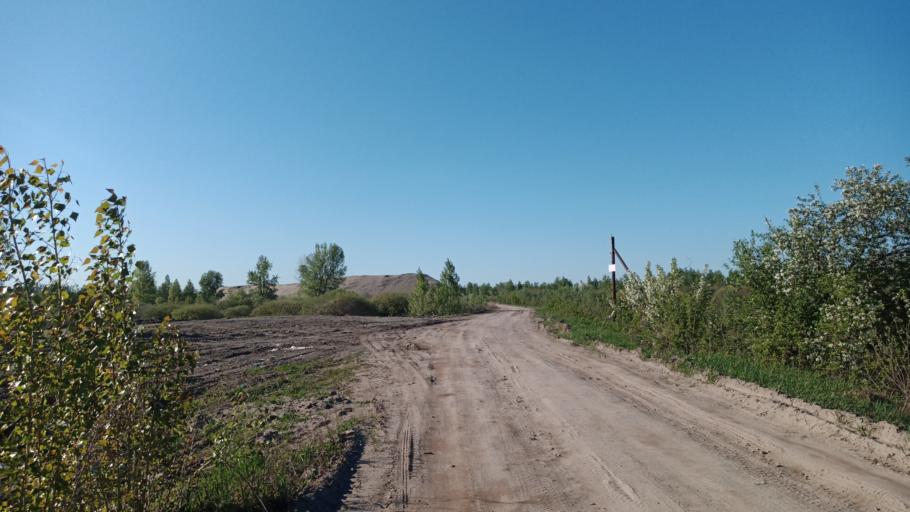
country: RU
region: Altai Krai
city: Zaton
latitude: 53.3078
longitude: 83.8240
